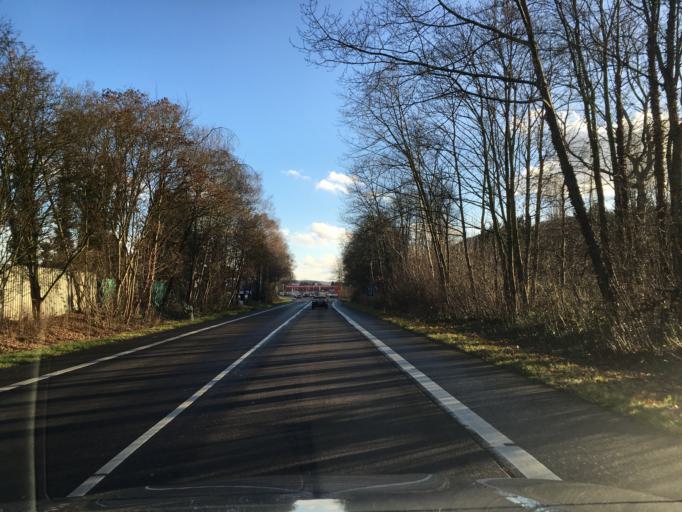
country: DE
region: North Rhine-Westphalia
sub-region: Regierungsbezirk Koln
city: Konigswinter
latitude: 50.6543
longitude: 7.1958
